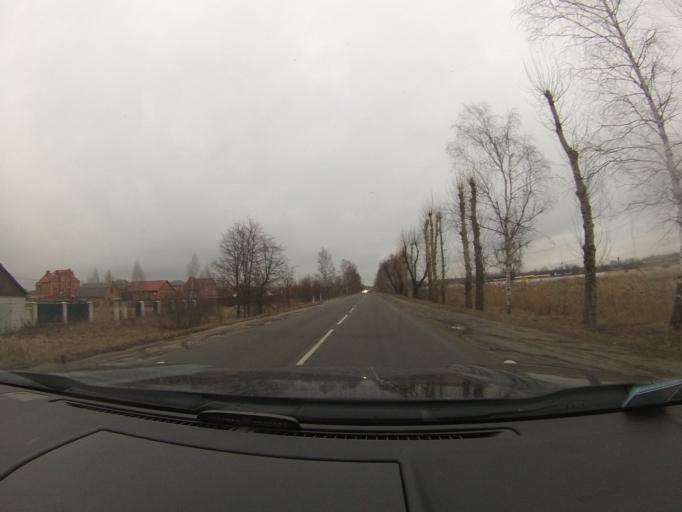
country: RU
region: Moskovskaya
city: Lopatinskiy
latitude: 55.3293
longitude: 38.7221
